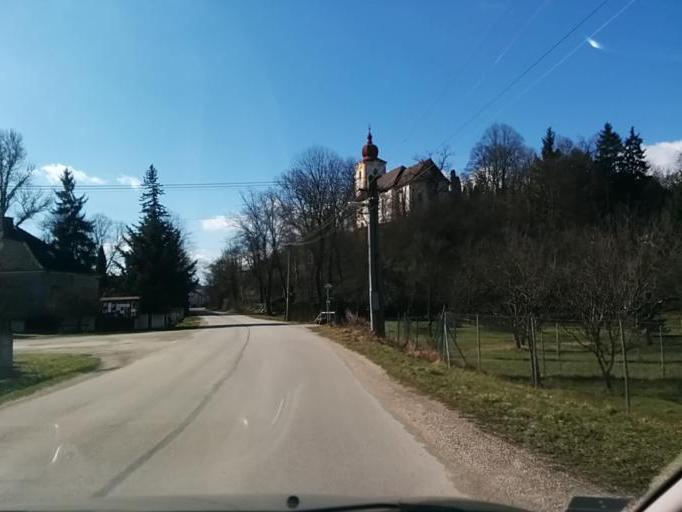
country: SK
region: Nitriansky
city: Cachtice
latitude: 48.7143
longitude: 17.7271
